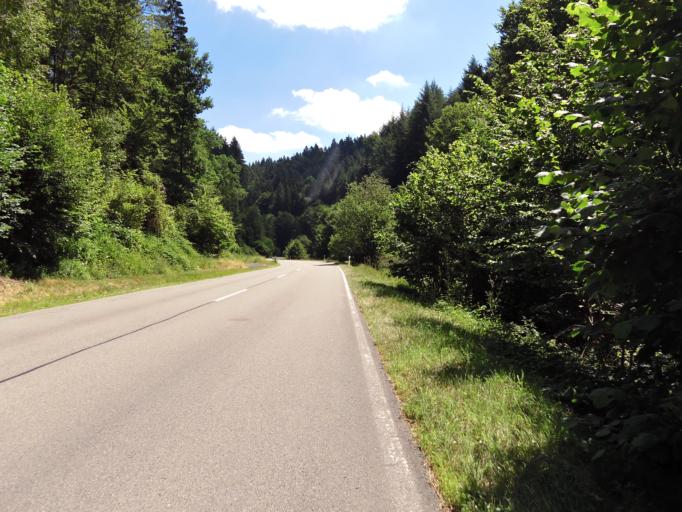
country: DE
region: Rheinland-Pfalz
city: Elmstein
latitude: 49.3557
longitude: 7.8926
